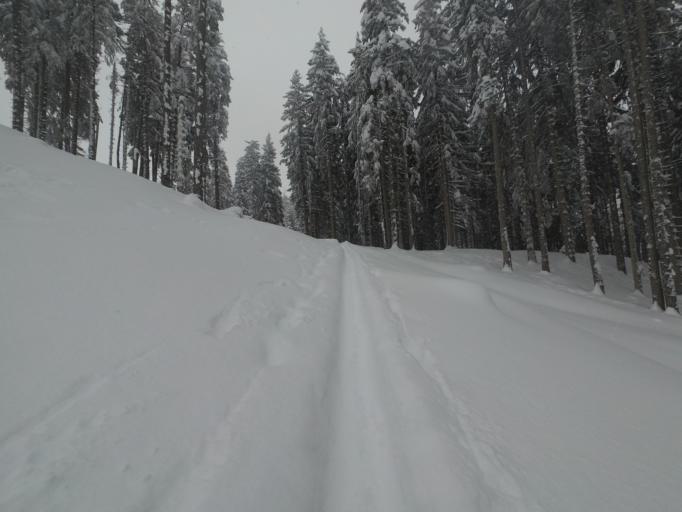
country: AT
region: Salzburg
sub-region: Politischer Bezirk Sankt Johann im Pongau
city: Sankt Johann im Pongau
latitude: 47.3108
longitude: 13.2162
